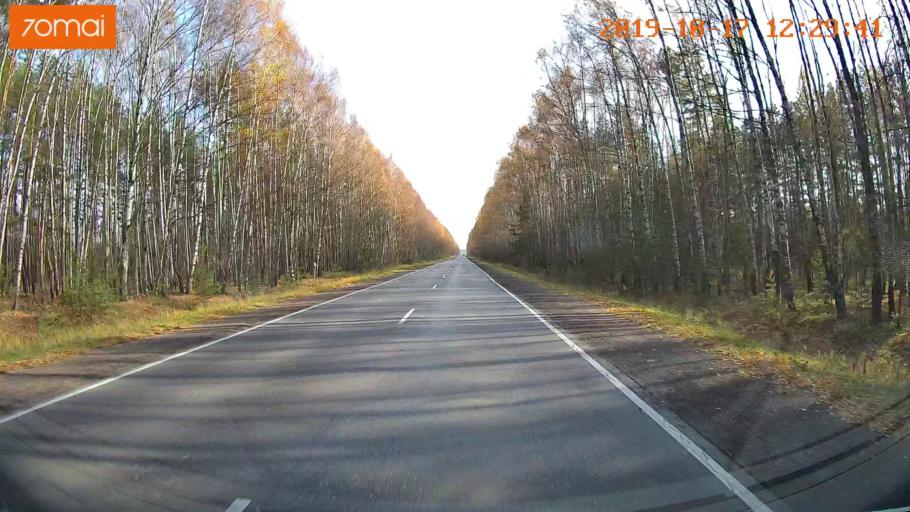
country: RU
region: Rjazan
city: Syntul
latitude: 54.9799
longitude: 41.2979
